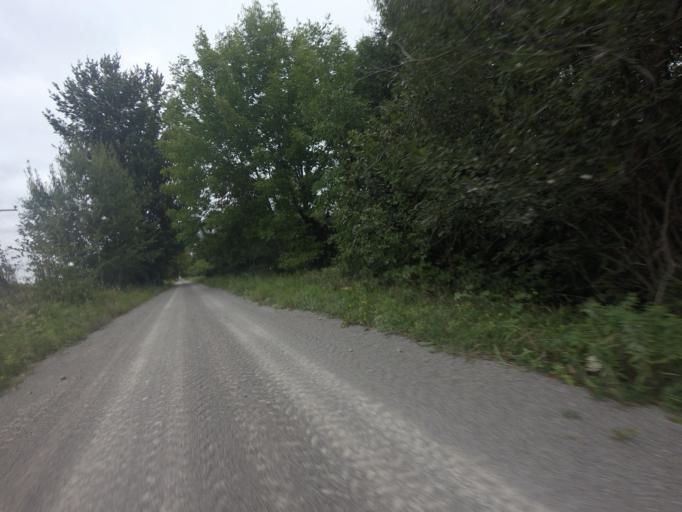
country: CA
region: Ontario
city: Omemee
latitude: 44.4690
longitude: -78.7525
